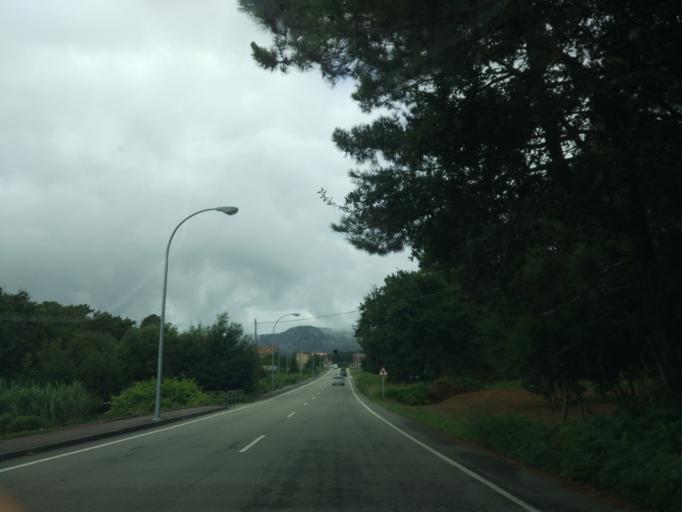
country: ES
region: Galicia
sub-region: Provincia da Coruna
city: Boiro
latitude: 42.6435
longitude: -8.8698
